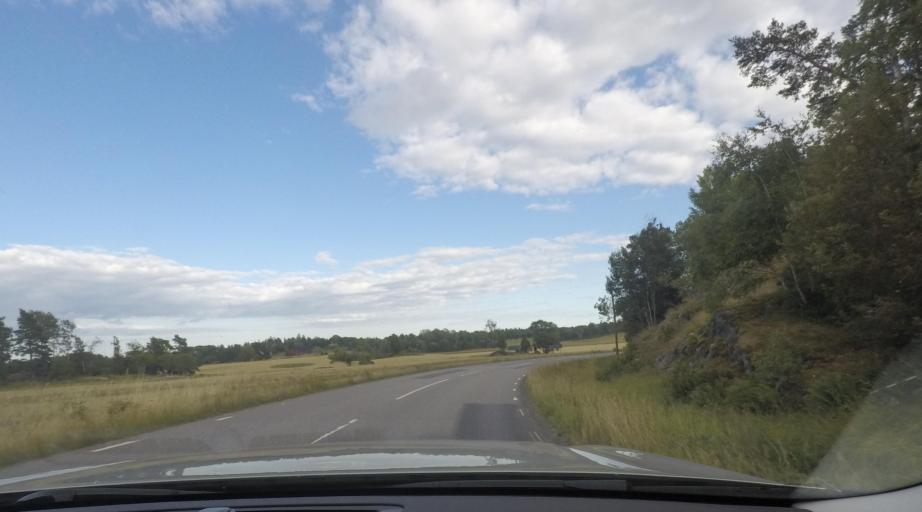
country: SE
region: Soedermanland
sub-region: Trosa Kommun
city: Trosa
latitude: 58.9935
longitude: 17.6757
